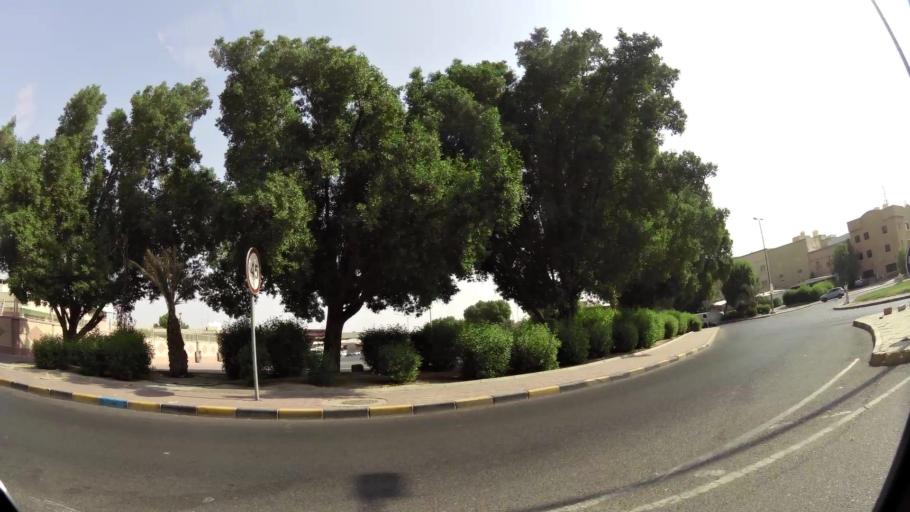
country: KW
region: Muhafazat al Jahra'
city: Al Jahra'
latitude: 29.3292
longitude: 47.6600
